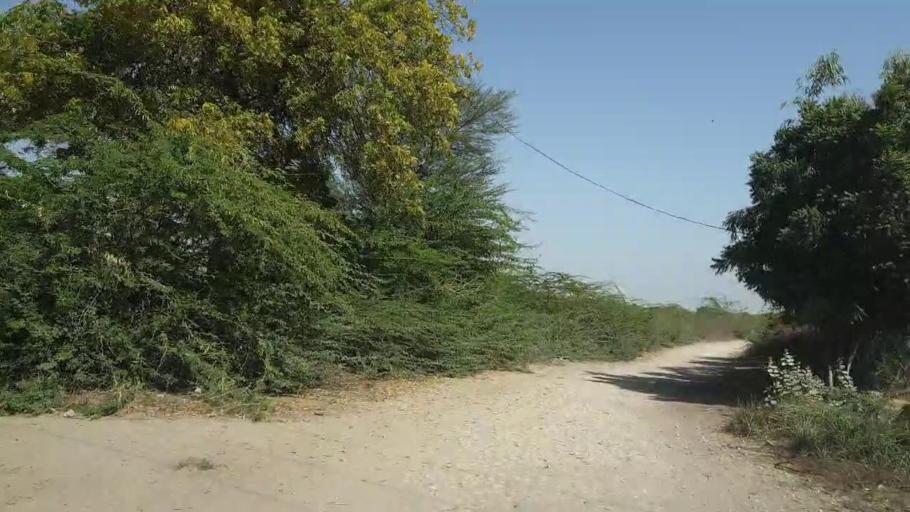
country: PK
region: Sindh
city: Naukot
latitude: 24.9614
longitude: 69.4923
